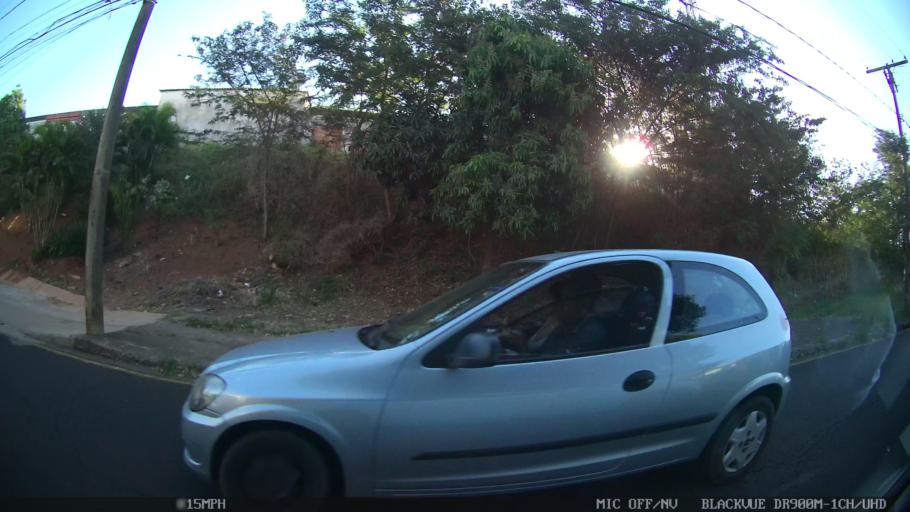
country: BR
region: Sao Paulo
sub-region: Sao Jose Do Rio Preto
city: Sao Jose do Rio Preto
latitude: -20.7966
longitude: -49.3578
